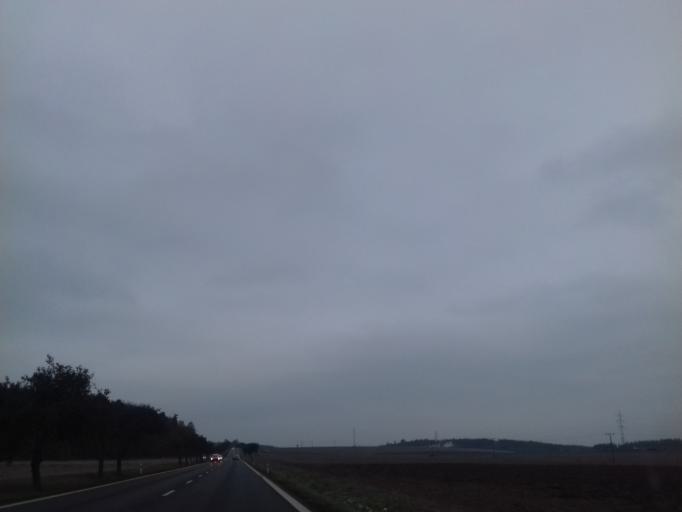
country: CZ
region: Plzensky
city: Stod
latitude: 49.6220
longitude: 13.1430
